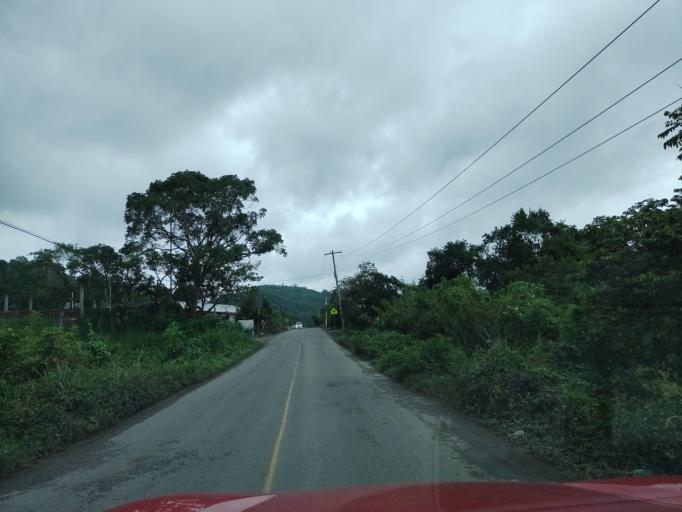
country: MX
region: Puebla
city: Espinal
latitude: 20.2603
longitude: -97.3754
